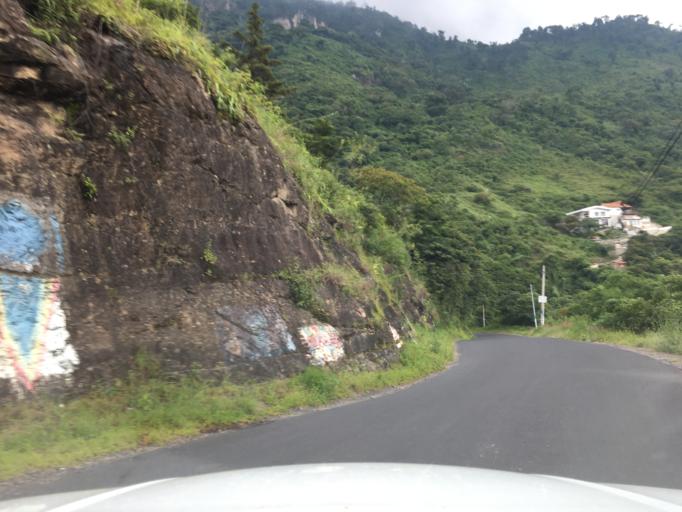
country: GT
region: Solola
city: Panajachel
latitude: 14.7326
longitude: -91.1438
